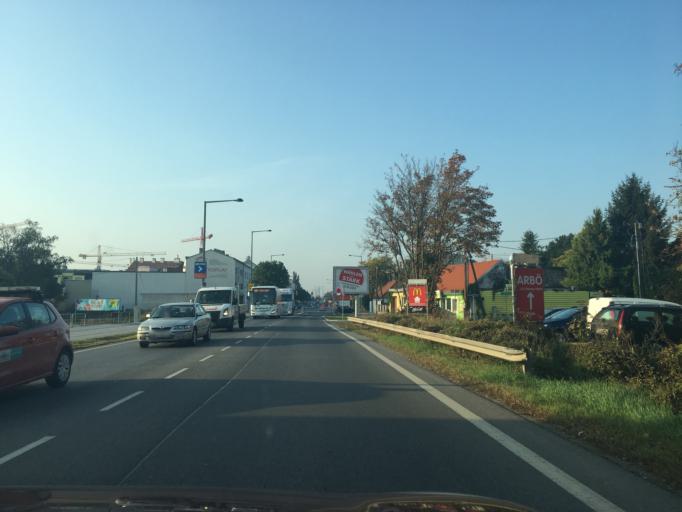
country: AT
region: Lower Austria
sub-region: Politischer Bezirk Korneuburg
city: Hagenbrunn
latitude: 48.3003
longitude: 16.4223
